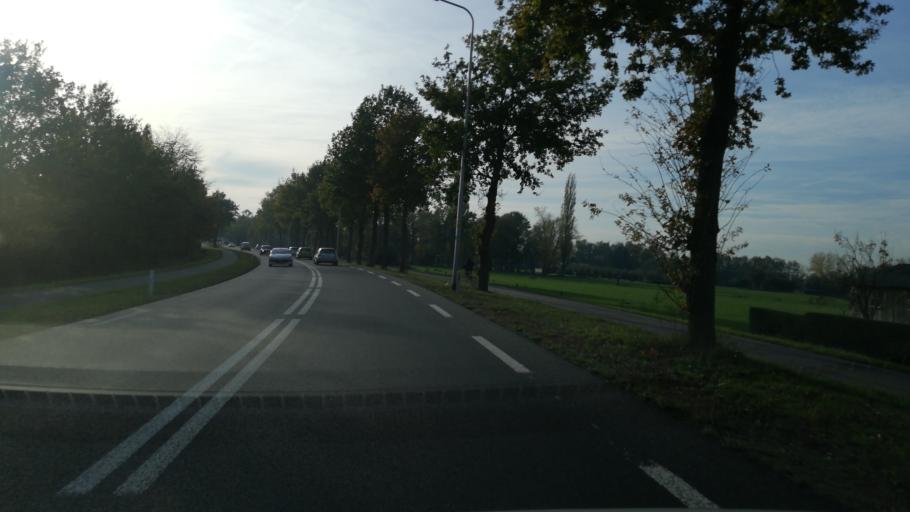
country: NL
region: Gelderland
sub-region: Gemeente Apeldoorn
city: Apeldoorn
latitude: 52.2305
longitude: 6.0229
